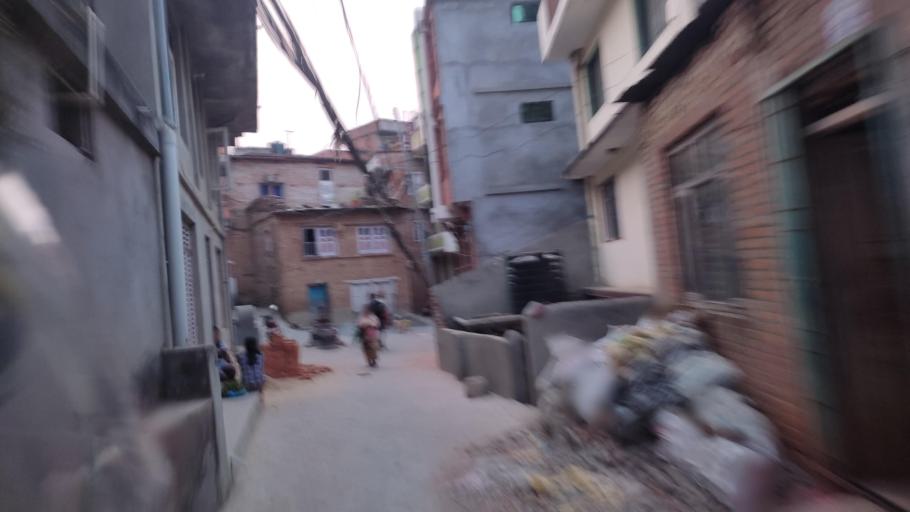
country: NP
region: Central Region
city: Kirtipur
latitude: 27.6709
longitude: 85.2855
